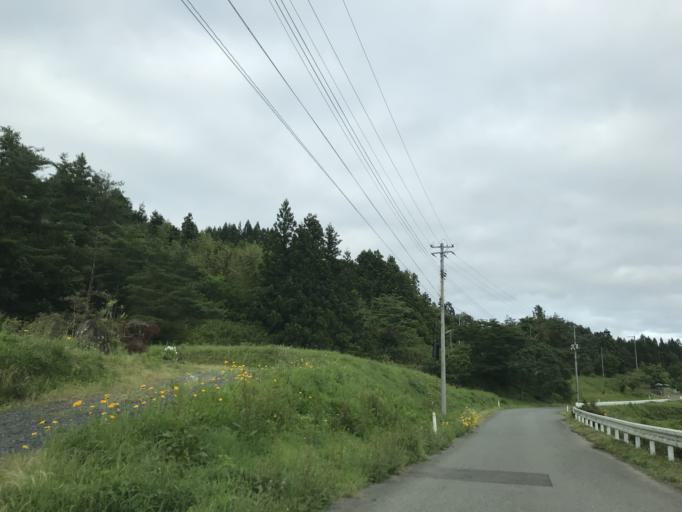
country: JP
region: Iwate
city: Ichinoseki
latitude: 38.8260
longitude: 141.2310
